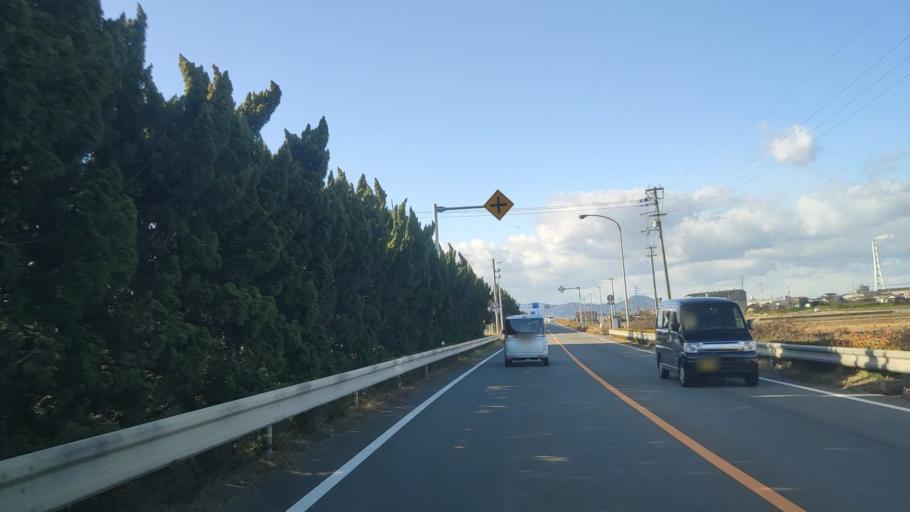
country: JP
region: Ehime
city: Saijo
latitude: 33.9166
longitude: 133.1290
